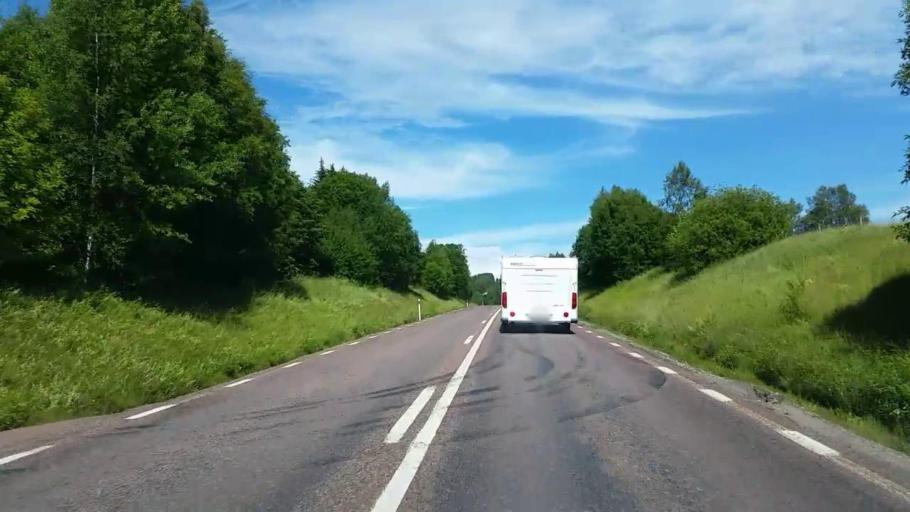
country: SE
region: Dalarna
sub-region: Rattviks Kommun
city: Raettvik
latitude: 60.9959
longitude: 15.2177
